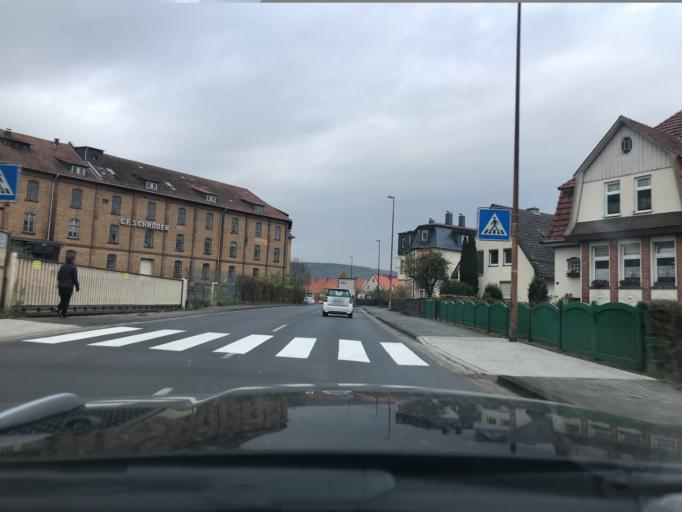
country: DE
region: Lower Saxony
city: Hannoversch Munden
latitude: 51.4071
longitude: 9.6421
